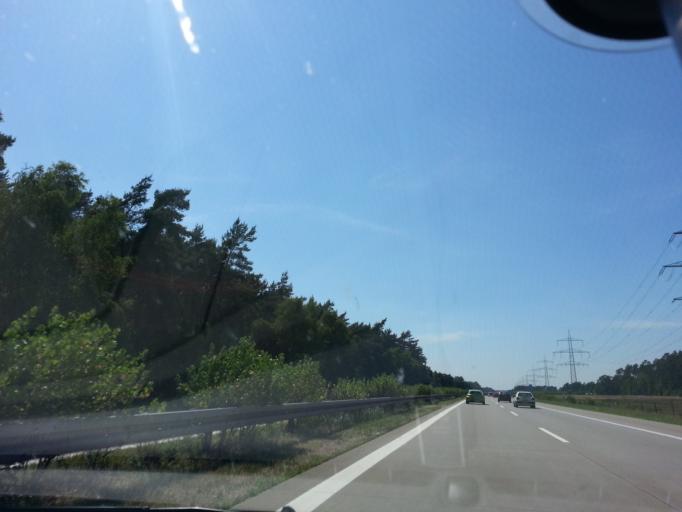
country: DE
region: Mecklenburg-Vorpommern
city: Zarrentin
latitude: 53.5112
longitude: 10.9085
